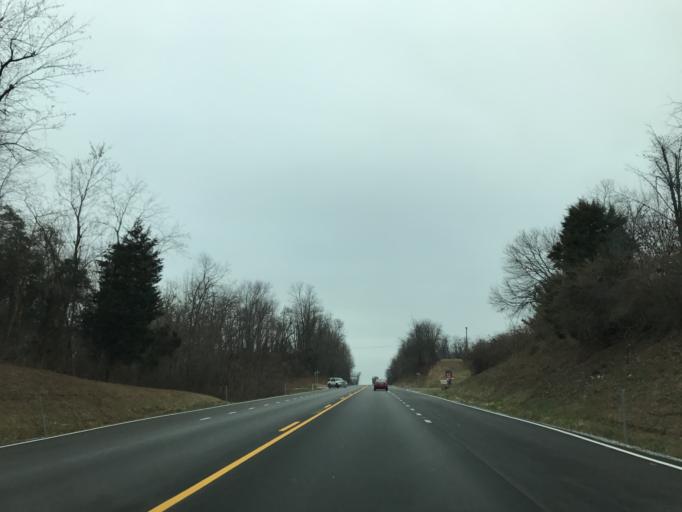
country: US
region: Maryland
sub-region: Carroll County
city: Westminster
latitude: 39.6010
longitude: -77.0497
